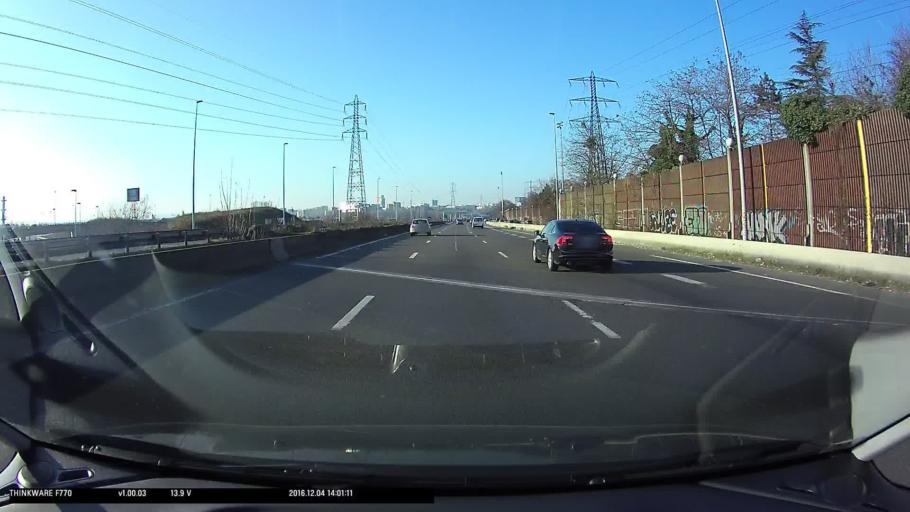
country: FR
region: Ile-de-France
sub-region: Departement du Val-d'Oise
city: Saint-Ouen-l'Aumone
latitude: 49.0330
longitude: 2.1088
